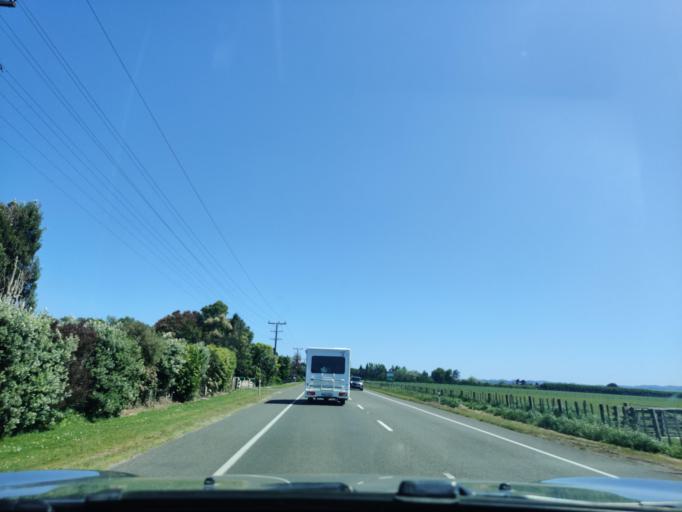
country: NZ
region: Manawatu-Wanganui
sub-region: Wanganui District
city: Wanganui
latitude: -39.8747
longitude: 174.9961
